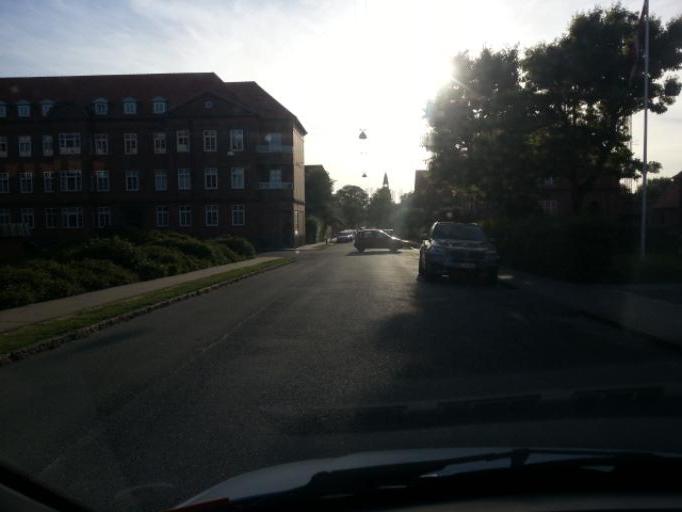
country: DK
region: South Denmark
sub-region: Esbjerg Kommune
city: Esbjerg
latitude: 55.4708
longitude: 8.4492
